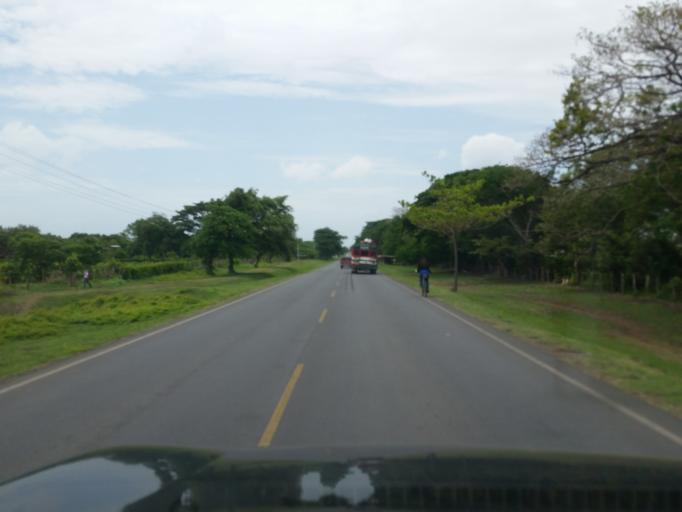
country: NI
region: Granada
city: Nandaime
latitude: 11.7393
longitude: -86.0214
